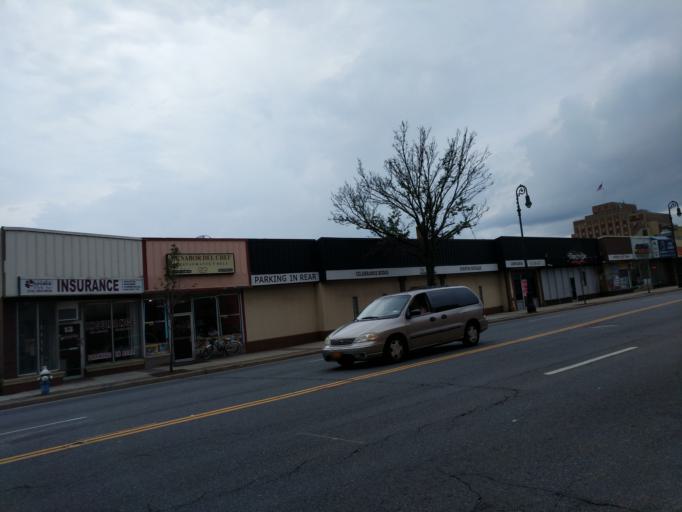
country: US
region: New York
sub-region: Nassau County
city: Hempstead
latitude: 40.7061
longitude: -73.6262
